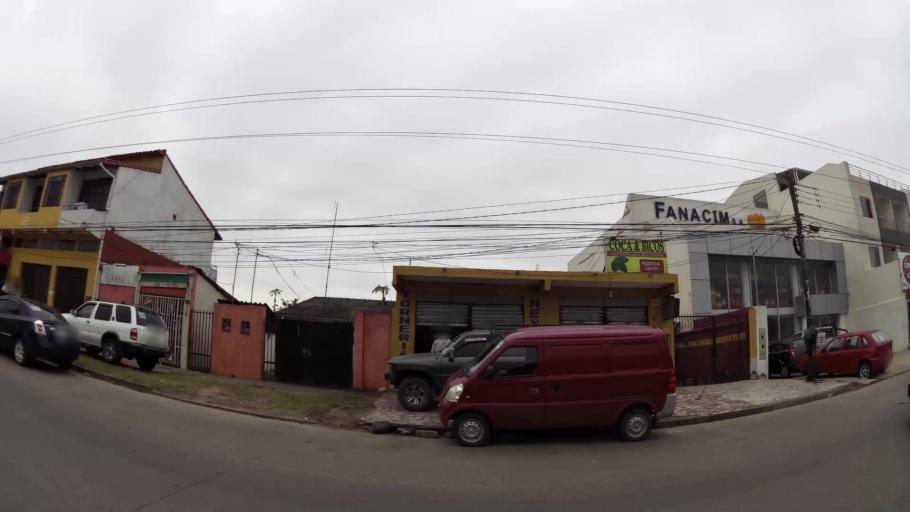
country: BO
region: Santa Cruz
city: Santa Cruz de la Sierra
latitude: -17.7530
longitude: -63.1602
